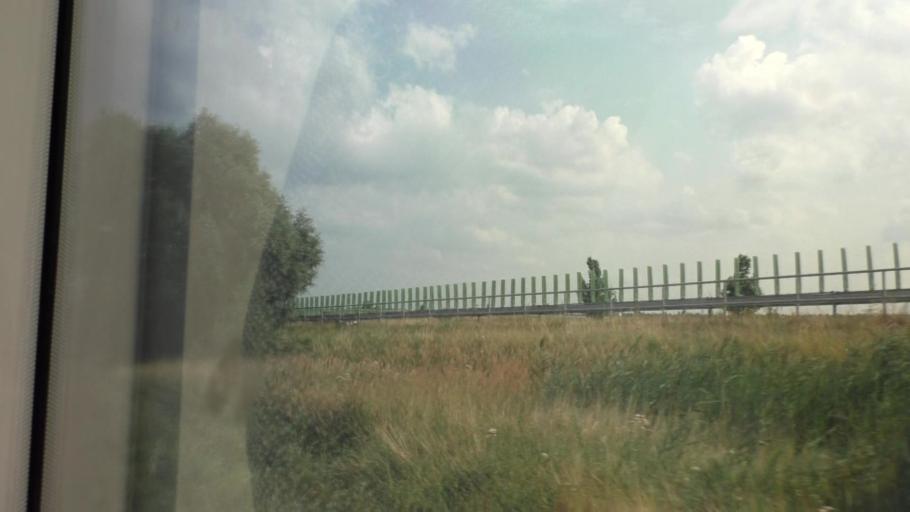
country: DE
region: Brandenburg
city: Beeskow
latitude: 52.1693
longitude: 14.2140
